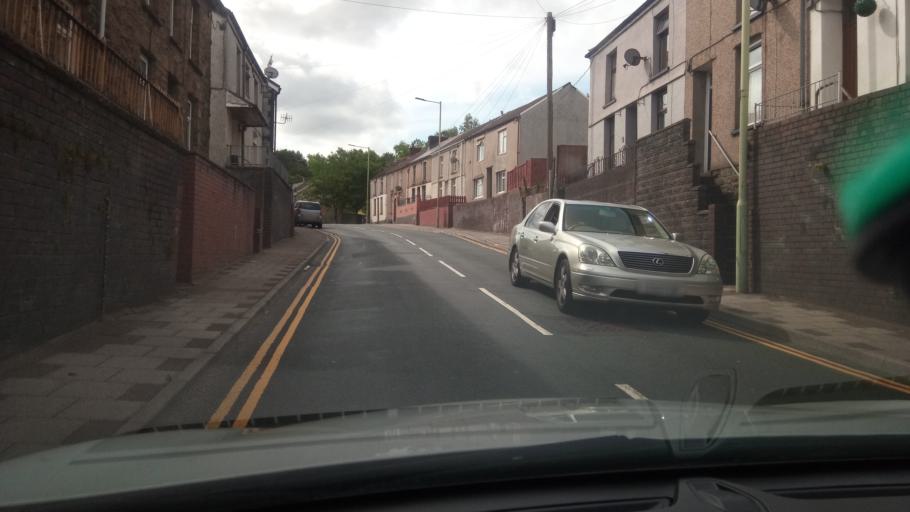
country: GB
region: Wales
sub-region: Rhondda Cynon Taf
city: Tonypandy
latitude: 51.6110
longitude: -3.4473
